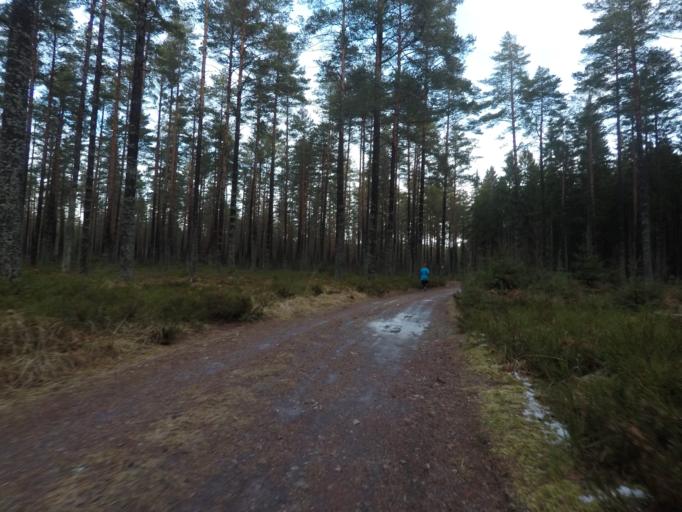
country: SE
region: Vaestmanland
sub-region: Kungsors Kommun
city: Kungsoer
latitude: 59.3589
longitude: 16.1165
